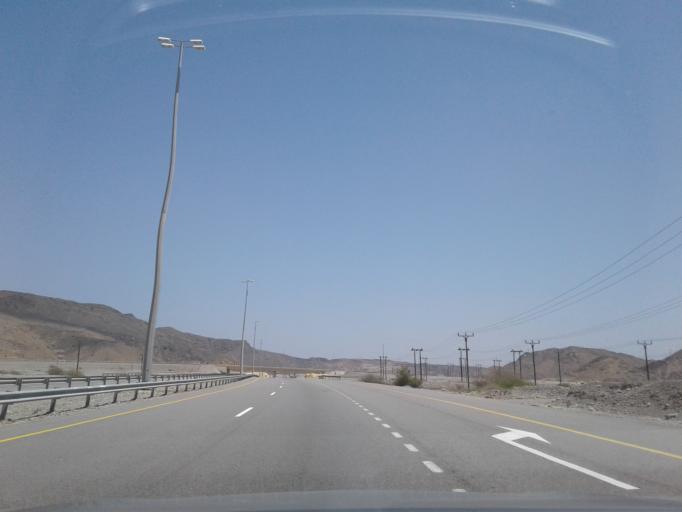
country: OM
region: Muhafazat Masqat
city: Muscat
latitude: 23.2486
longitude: 58.7860
